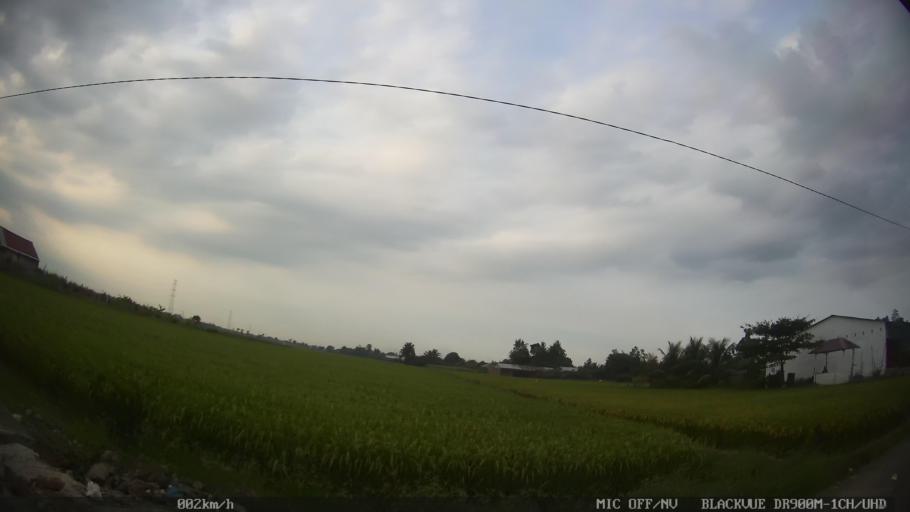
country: ID
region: North Sumatra
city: Sunggal
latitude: 3.5611
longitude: 98.5923
